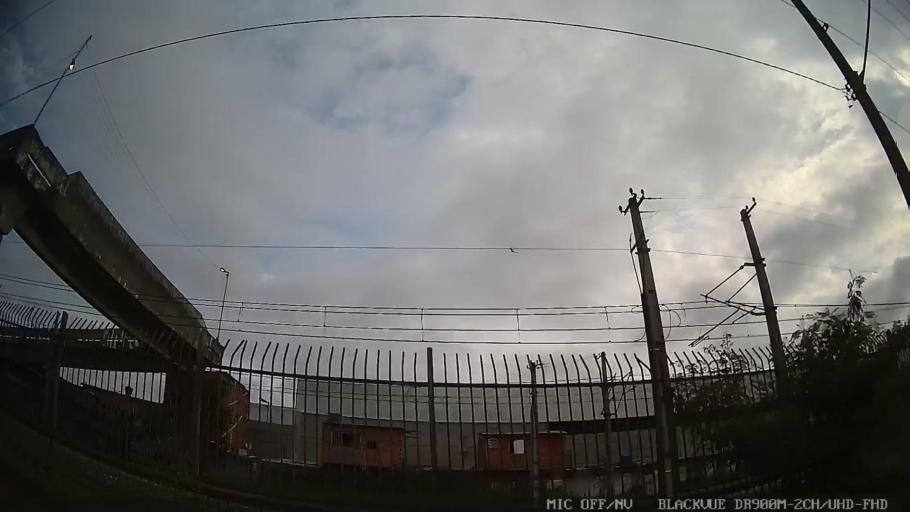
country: BR
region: Sao Paulo
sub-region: Ferraz De Vasconcelos
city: Ferraz de Vasconcelos
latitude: -23.4934
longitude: -46.4127
